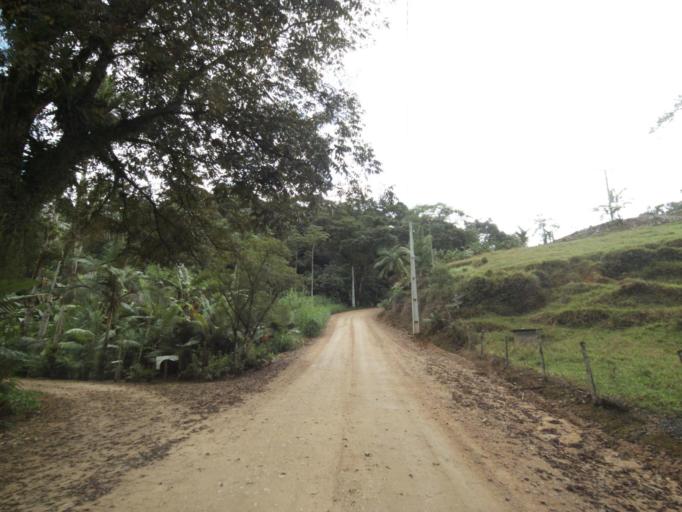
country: BR
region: Santa Catarina
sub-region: Pomerode
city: Pomerode
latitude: -26.7035
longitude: -49.2241
